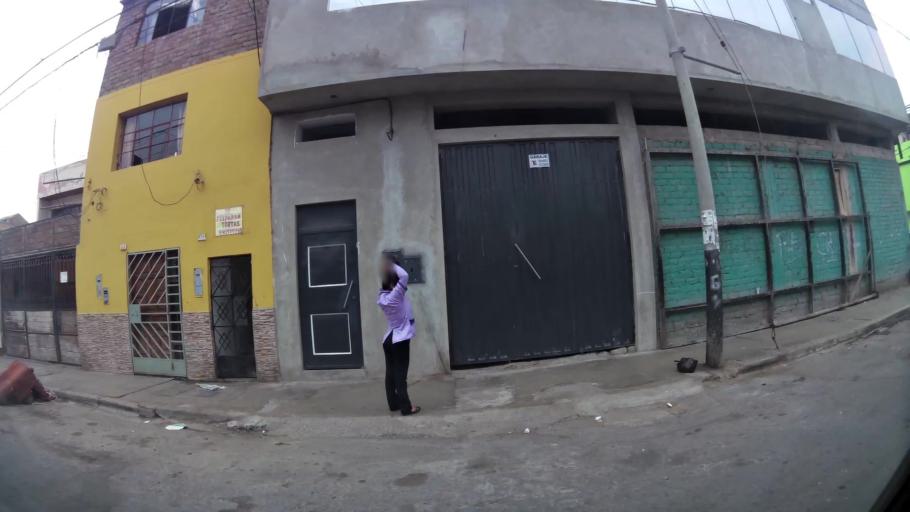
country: PE
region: La Libertad
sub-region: Provincia de Trujillo
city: Trujillo
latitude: -8.1155
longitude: -79.0189
